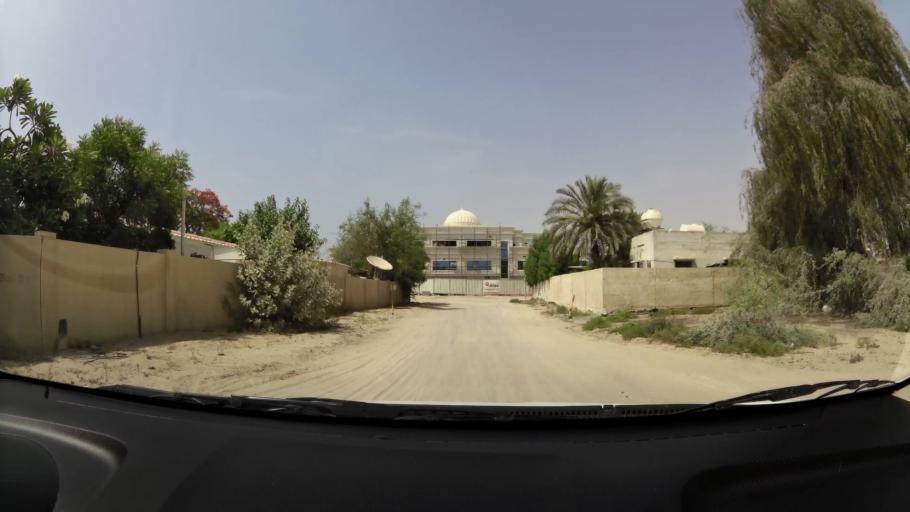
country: AE
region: Ash Shariqah
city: Sharjah
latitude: 25.3525
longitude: 55.4092
